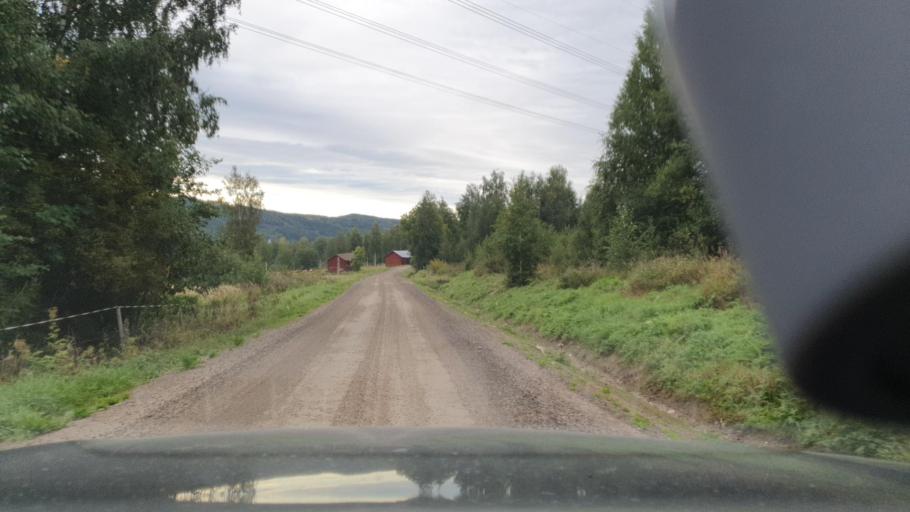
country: SE
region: Vaermland
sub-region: Torsby Kommun
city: Torsby
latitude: 59.9573
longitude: 12.8890
